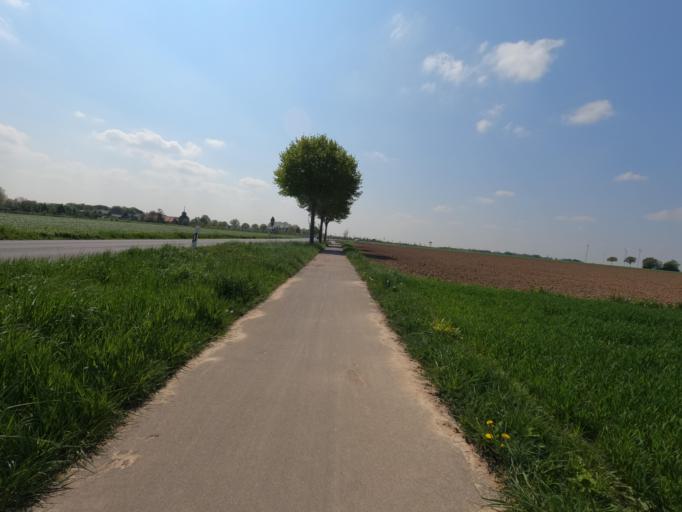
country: DE
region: North Rhine-Westphalia
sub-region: Regierungsbezirk Koln
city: Heinsberg
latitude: 51.0251
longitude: 6.0900
